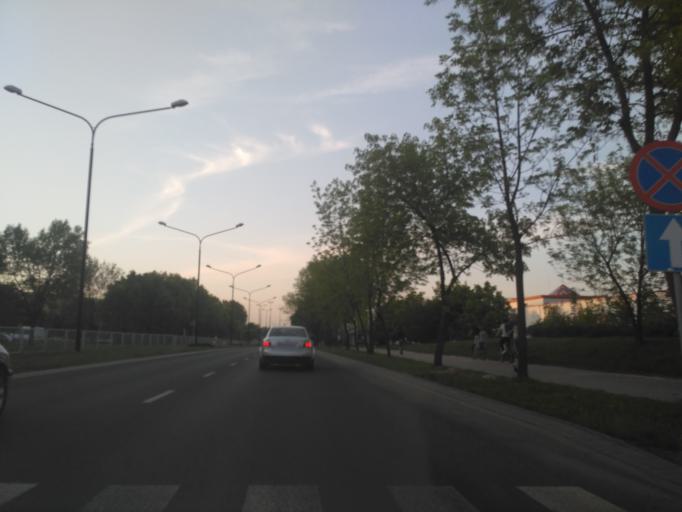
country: PL
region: Lublin Voivodeship
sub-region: Powiat lubelski
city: Lublin
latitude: 51.2651
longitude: 22.5584
